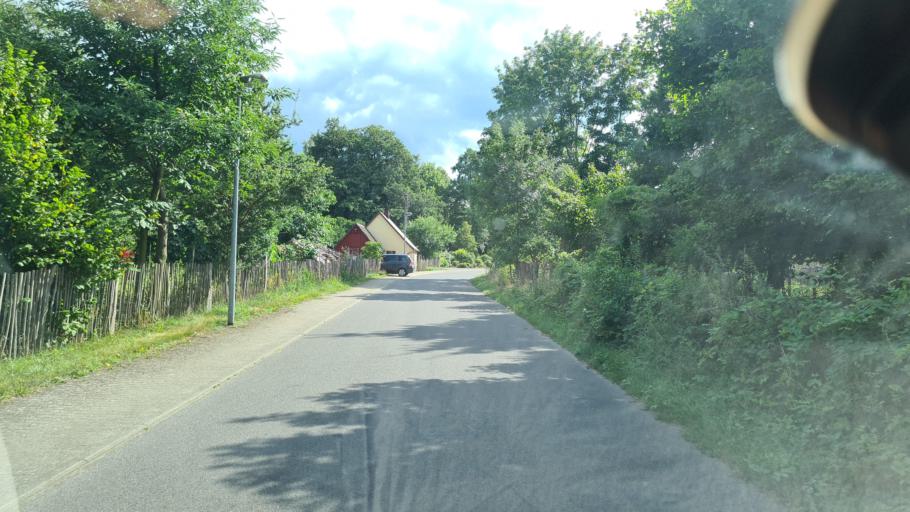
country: DE
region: Brandenburg
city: Neupetershain
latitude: 51.6309
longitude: 14.1306
